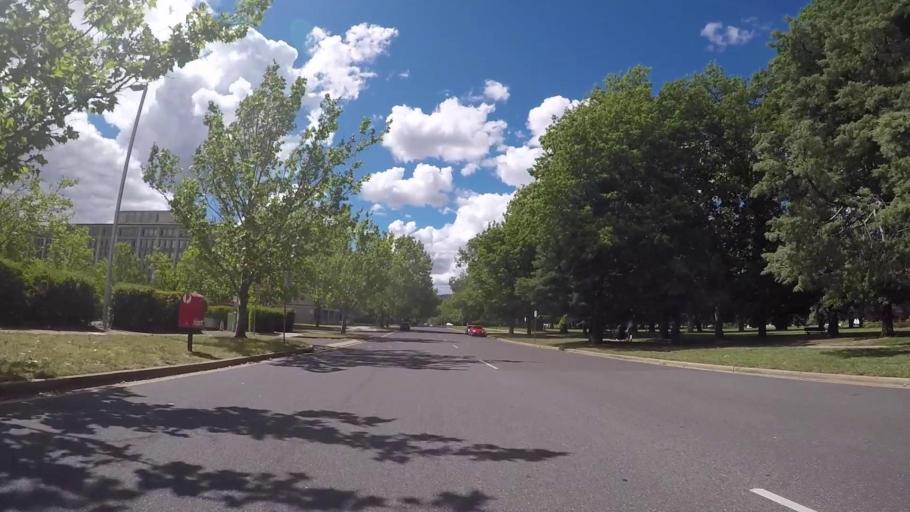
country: AU
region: Australian Capital Territory
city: Forrest
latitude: -35.3000
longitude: 149.1285
